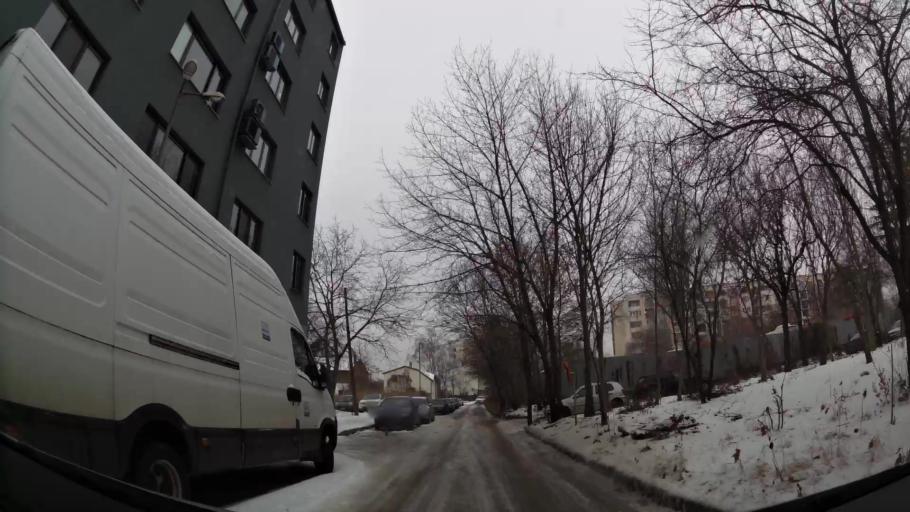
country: BG
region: Sofia-Capital
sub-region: Stolichna Obshtina
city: Sofia
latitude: 42.7081
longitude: 23.3017
